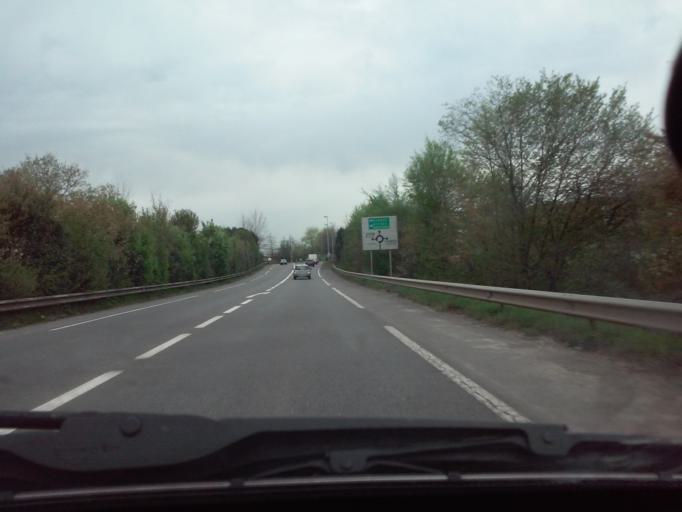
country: FR
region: Brittany
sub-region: Departement d'Ille-et-Vilaine
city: Fougeres
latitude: 48.3378
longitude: -1.2077
